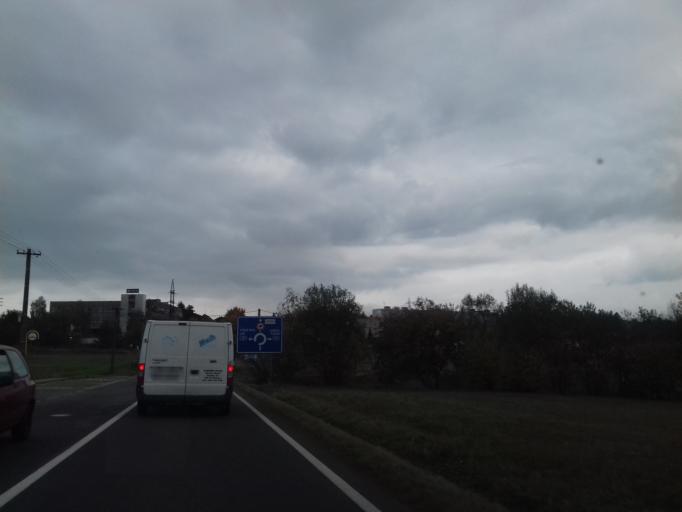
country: CZ
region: Pardubicky
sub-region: Okres Chrudim
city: Skutec
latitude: 49.8518
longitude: 15.9906
